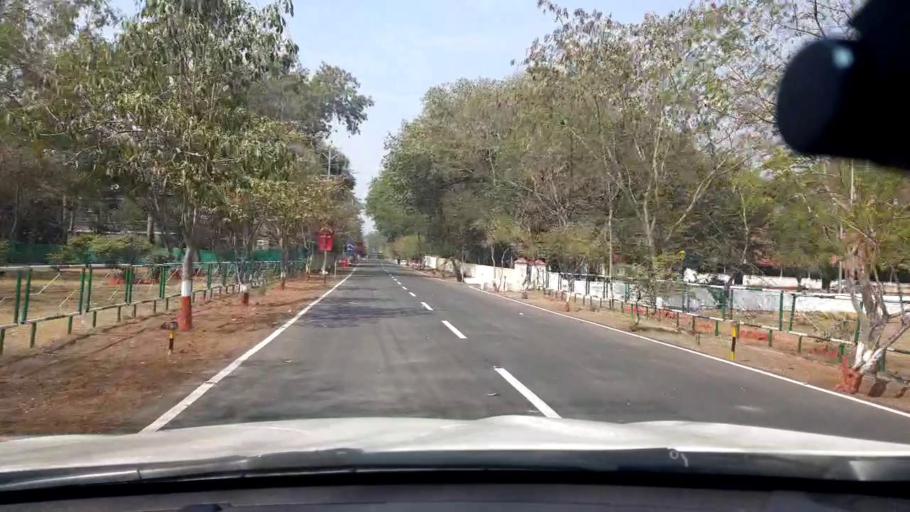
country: IN
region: Maharashtra
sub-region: Pune Division
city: Shivaji Nagar
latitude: 18.5459
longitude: 73.8634
